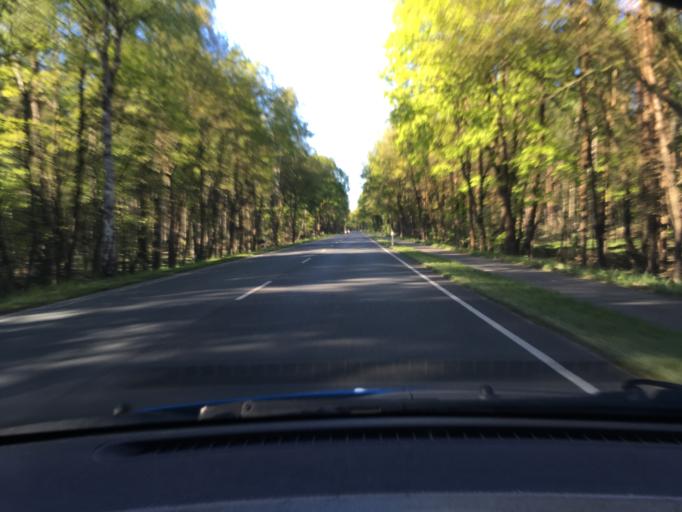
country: DE
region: Lower Saxony
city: Soltau
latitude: 53.0450
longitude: 9.8566
